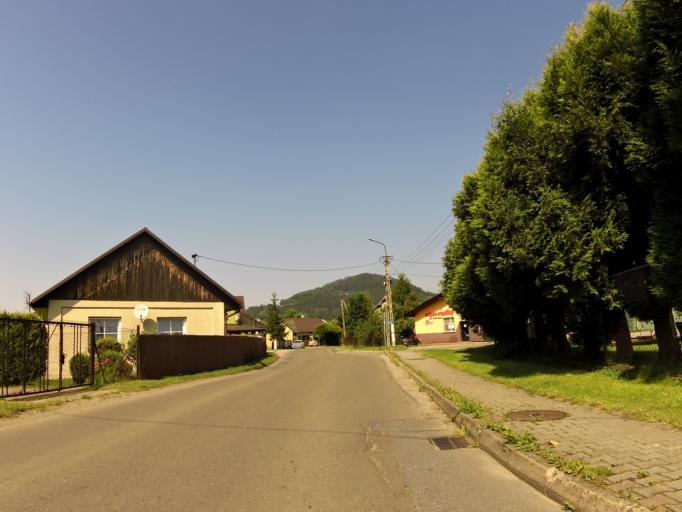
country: PL
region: Silesian Voivodeship
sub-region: Powiat zywiecki
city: Wieprz
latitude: 49.6454
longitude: 19.1783
